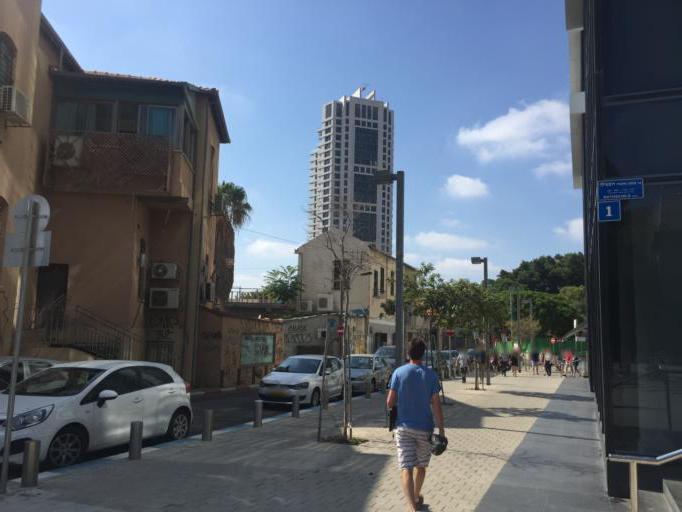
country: IL
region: Tel Aviv
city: Yafo
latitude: 32.0629
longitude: 34.7688
